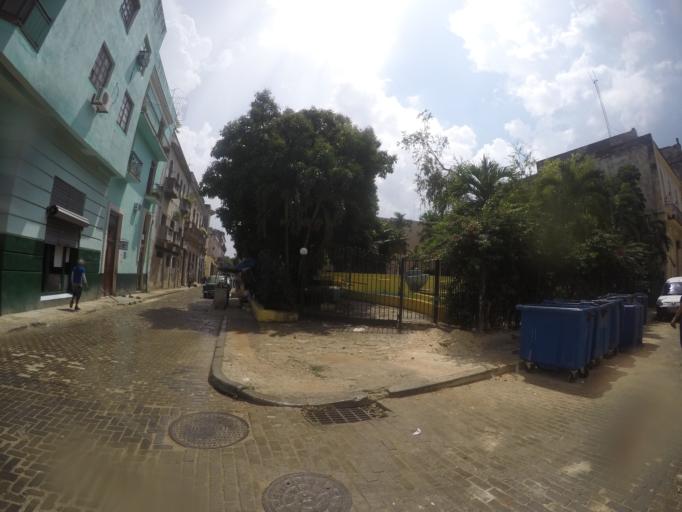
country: CU
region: La Habana
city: La Habana Vieja
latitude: 23.1354
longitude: -82.3483
